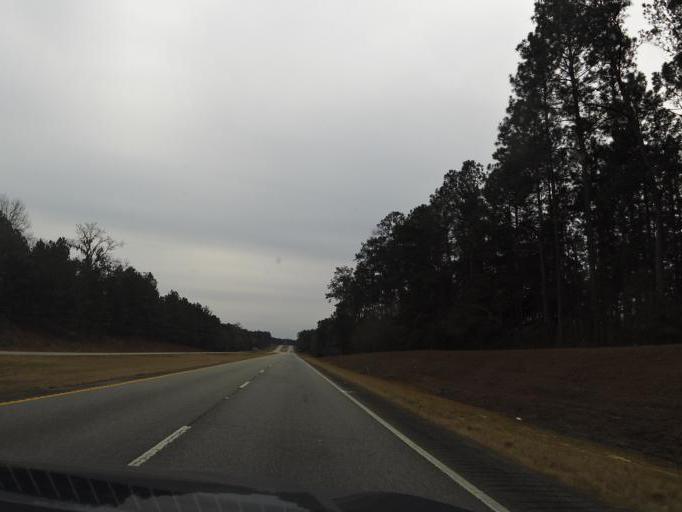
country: US
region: Georgia
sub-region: Thomas County
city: Boston
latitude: 30.7101
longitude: -83.8923
